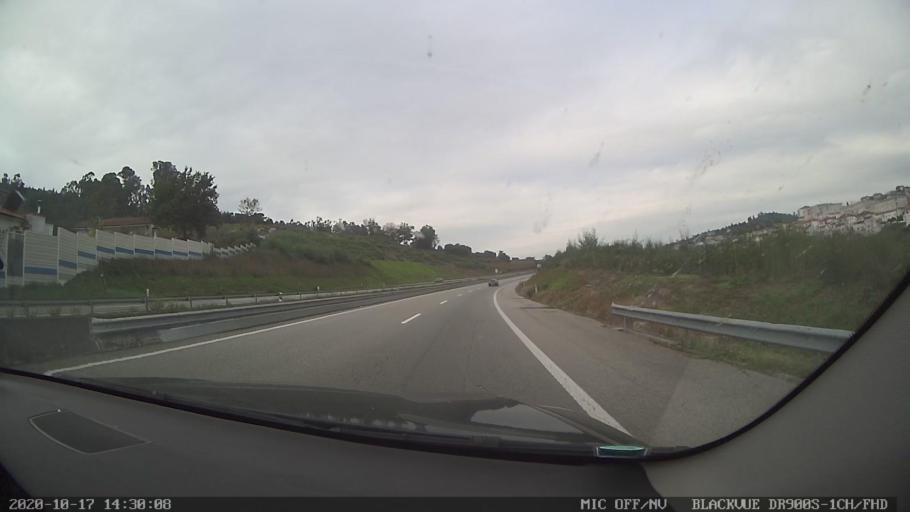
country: PT
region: Braga
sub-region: Guimaraes
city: Candoso
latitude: 41.4101
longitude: -8.3188
